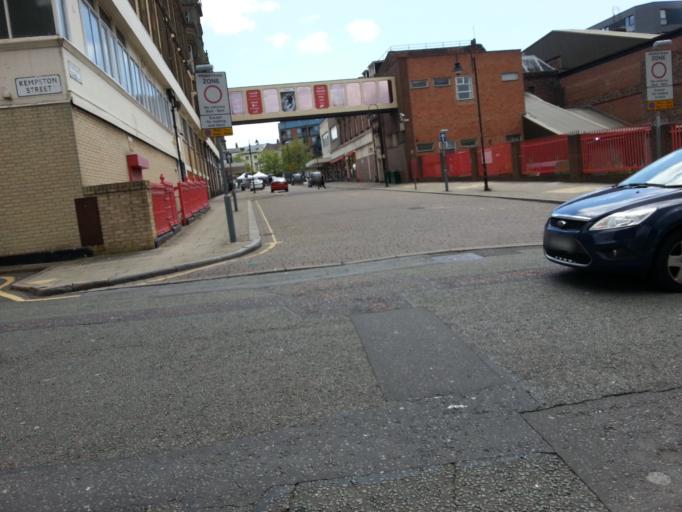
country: GB
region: England
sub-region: Liverpool
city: Liverpool
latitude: 53.4104
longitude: -2.9729
